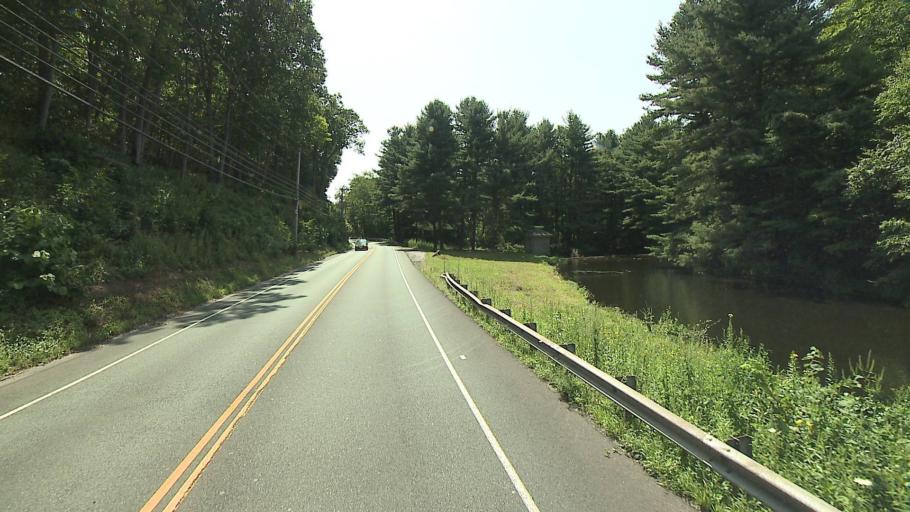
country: US
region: Connecticut
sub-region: Fairfield County
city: Trumbull
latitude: 41.3159
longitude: -73.2604
